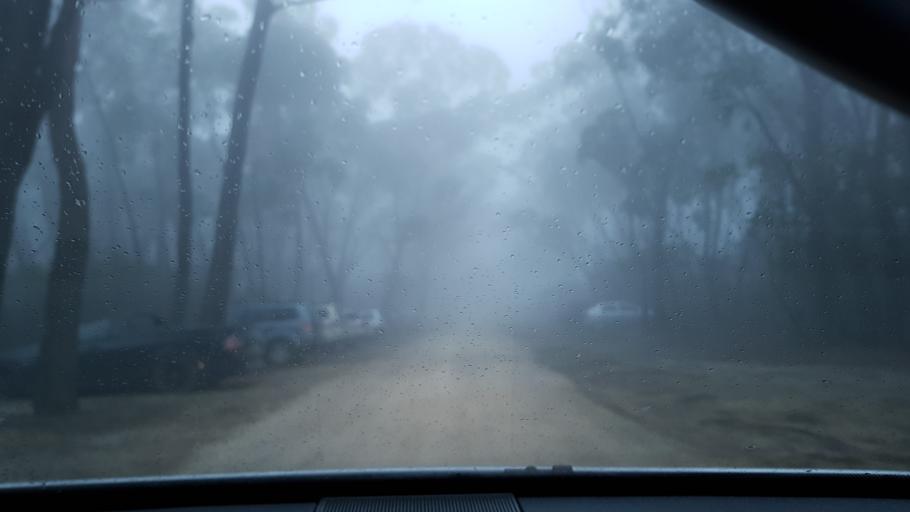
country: AU
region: New South Wales
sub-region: Blue Mountains Municipality
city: Katoomba
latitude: -33.9889
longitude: 150.1074
